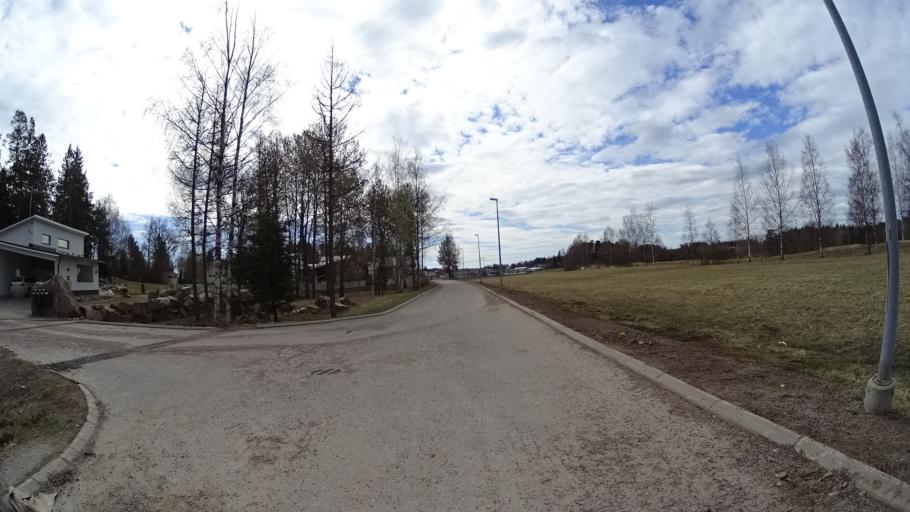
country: FI
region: Uusimaa
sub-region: Helsinki
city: Kauniainen
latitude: 60.2712
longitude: 24.7451
